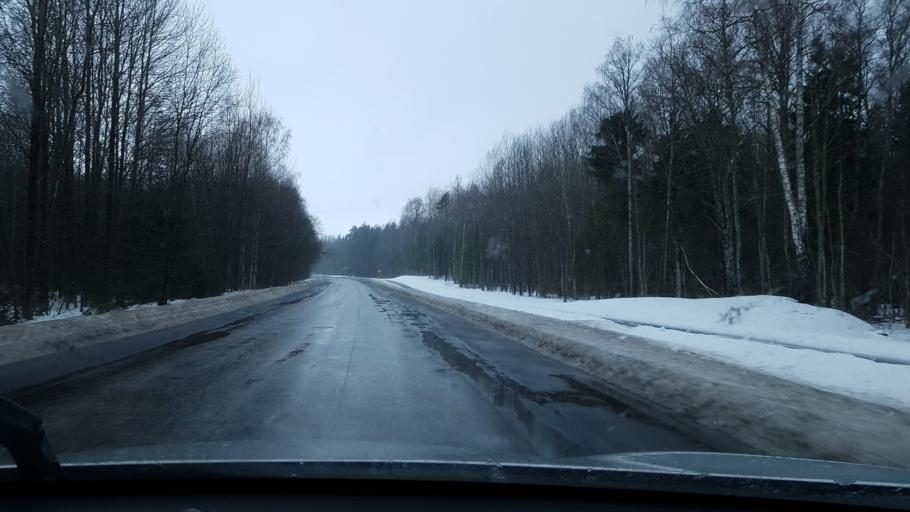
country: EE
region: Raplamaa
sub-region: Kohila vald
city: Kohila
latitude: 59.1688
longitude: 24.7131
